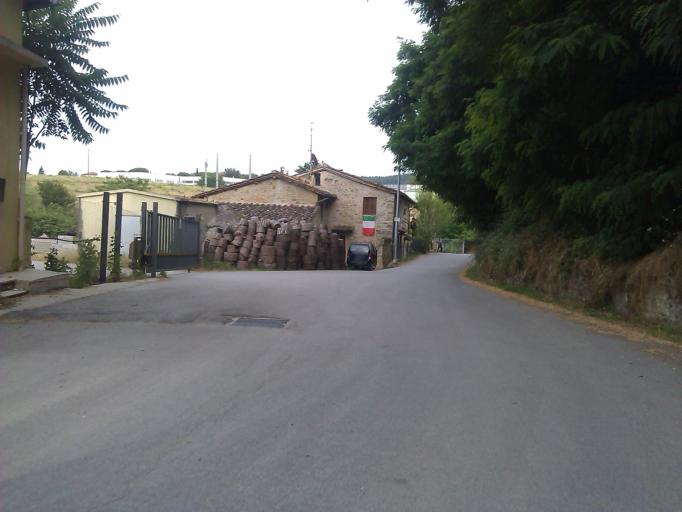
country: IT
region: Tuscany
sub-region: Province of Arezzo
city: Bucine
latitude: 43.4967
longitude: 11.6314
